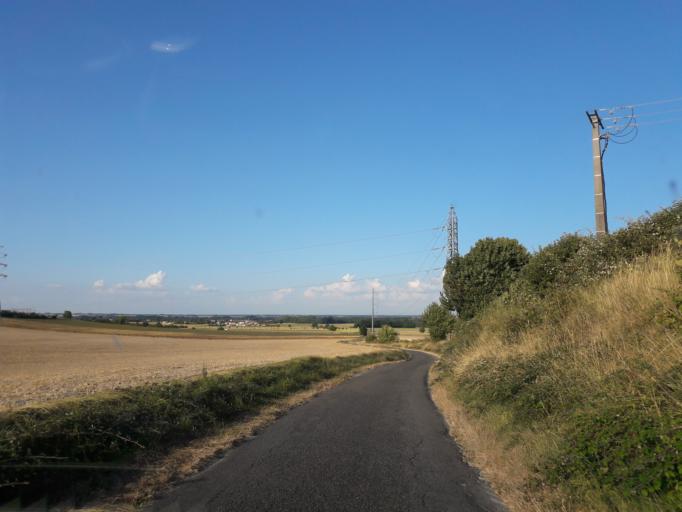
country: FR
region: Poitou-Charentes
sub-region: Departement de la Charente-Maritime
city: Thenac
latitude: 45.6653
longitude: -0.6050
